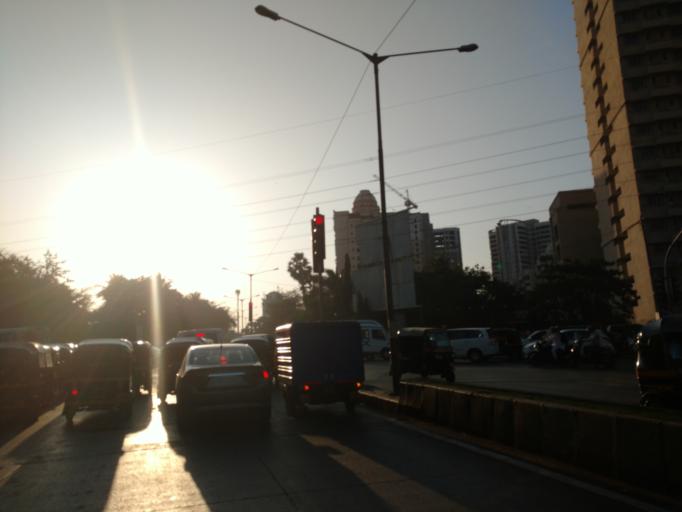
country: IN
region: Maharashtra
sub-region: Mumbai Suburban
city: Borivli
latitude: 19.2073
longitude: 72.8352
